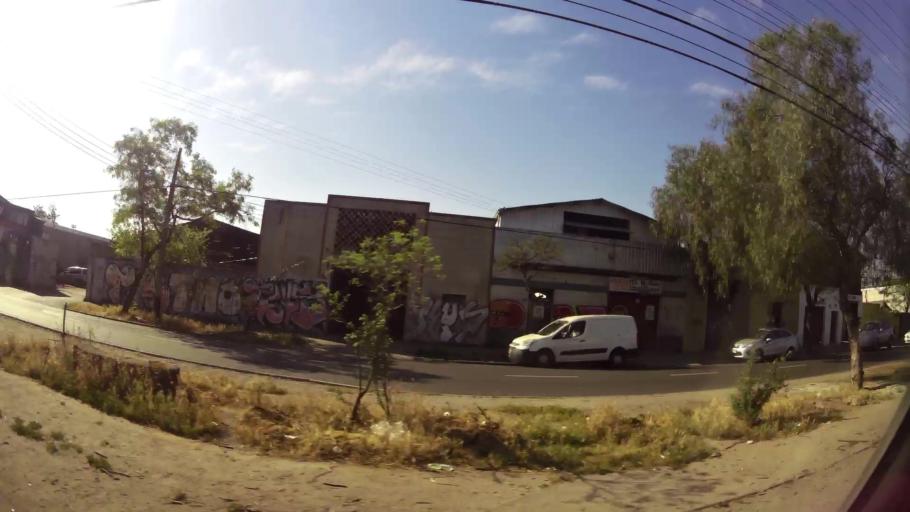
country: CL
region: Santiago Metropolitan
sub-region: Provincia de Santiago
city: Santiago
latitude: -33.4789
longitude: -70.6590
